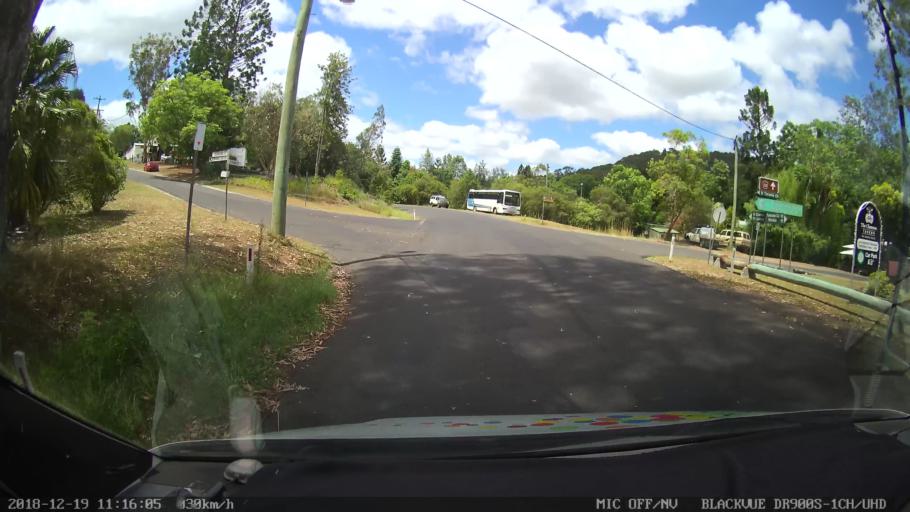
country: AU
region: New South Wales
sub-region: Lismore Municipality
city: Nimbin
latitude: -28.6723
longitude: 153.2779
